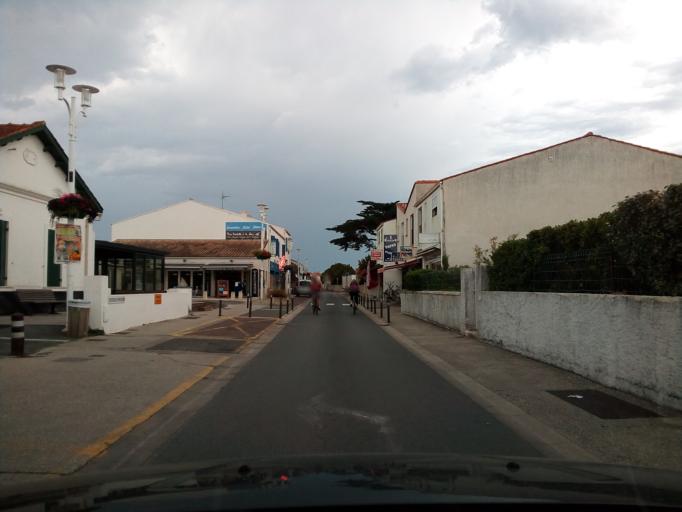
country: FR
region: Poitou-Charentes
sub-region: Departement de la Charente-Maritime
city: Dolus-d'Oleron
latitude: 45.9172
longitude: -1.3305
